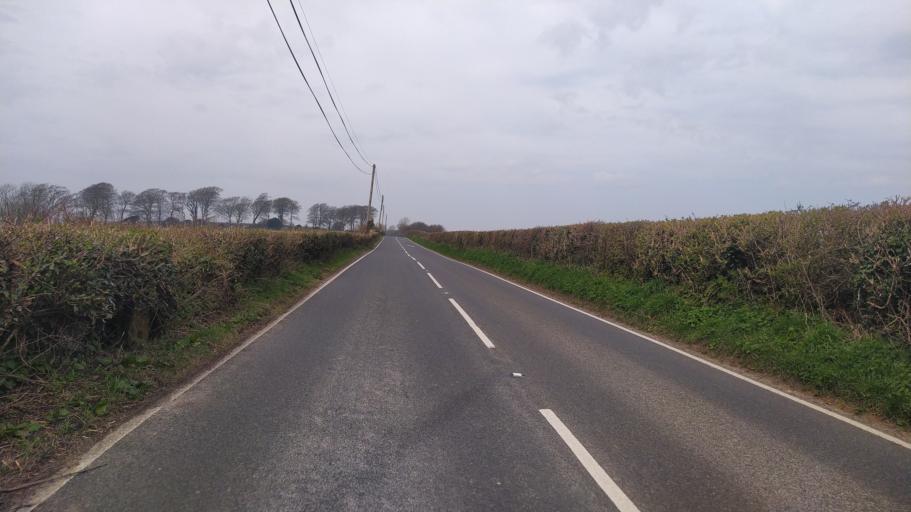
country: GB
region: England
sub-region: Dorset
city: Beaminster
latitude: 50.7804
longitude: -2.5946
